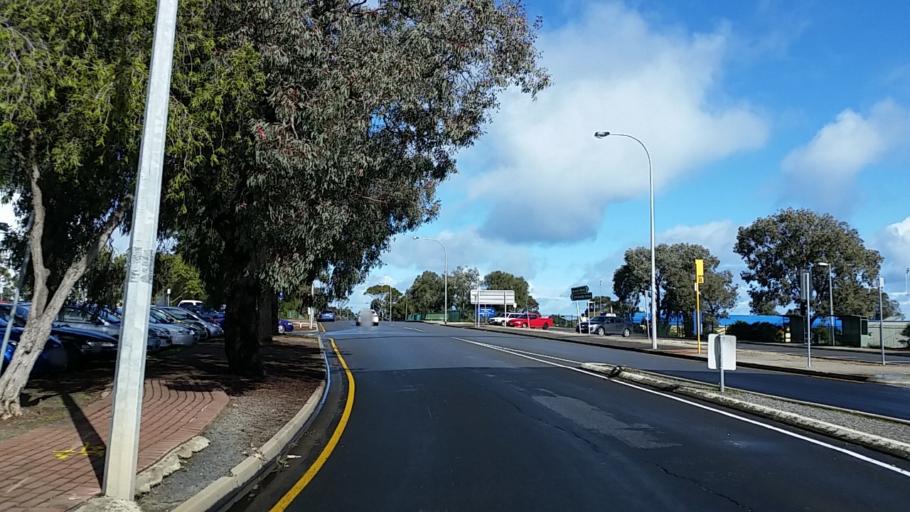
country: AU
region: South Australia
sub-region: Onkaparinga
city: Noarlunga Downs
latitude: -35.1395
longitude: 138.4933
